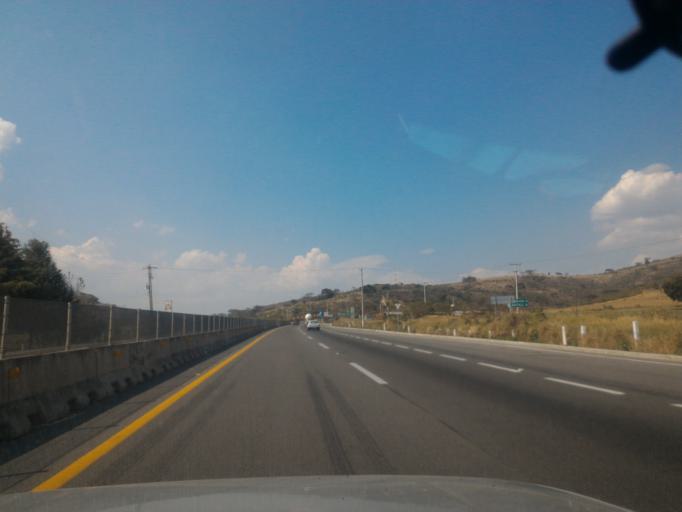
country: MX
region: Jalisco
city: San Andres Ixtlan
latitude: 19.8377
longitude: -103.5001
